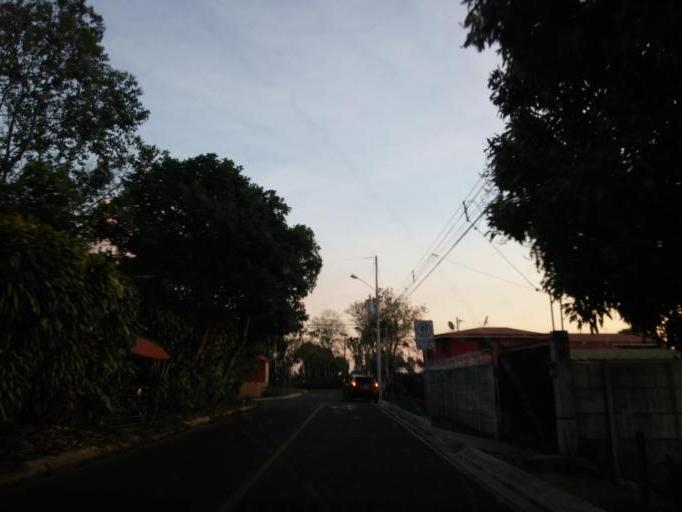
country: CR
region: Alajuela
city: Sabanilla
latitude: 10.0743
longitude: -84.2169
